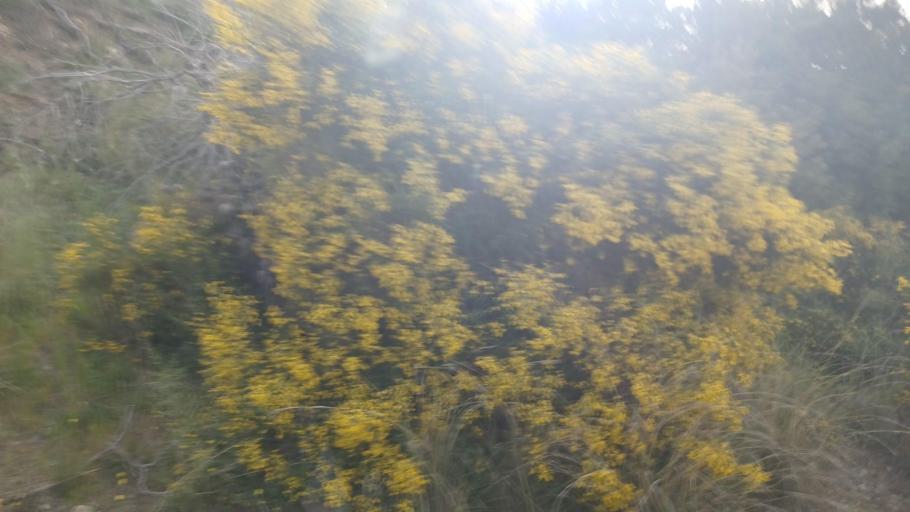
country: CY
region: Pafos
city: Polis
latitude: 34.9921
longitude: 32.3317
